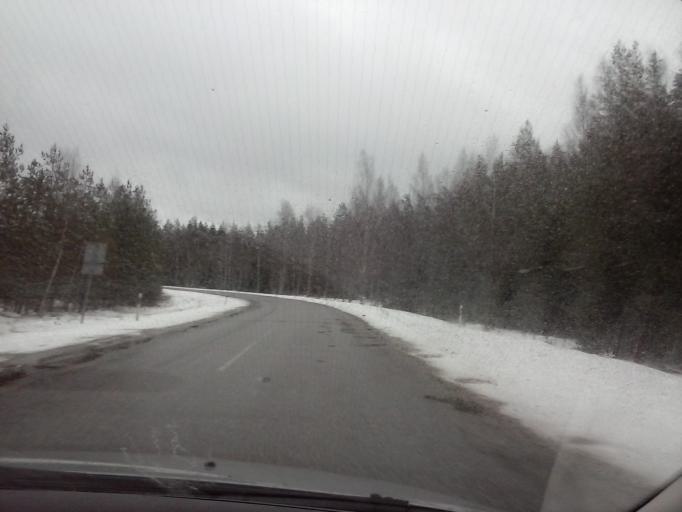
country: LV
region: Strenci
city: Seda
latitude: 57.6276
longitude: 25.7428
